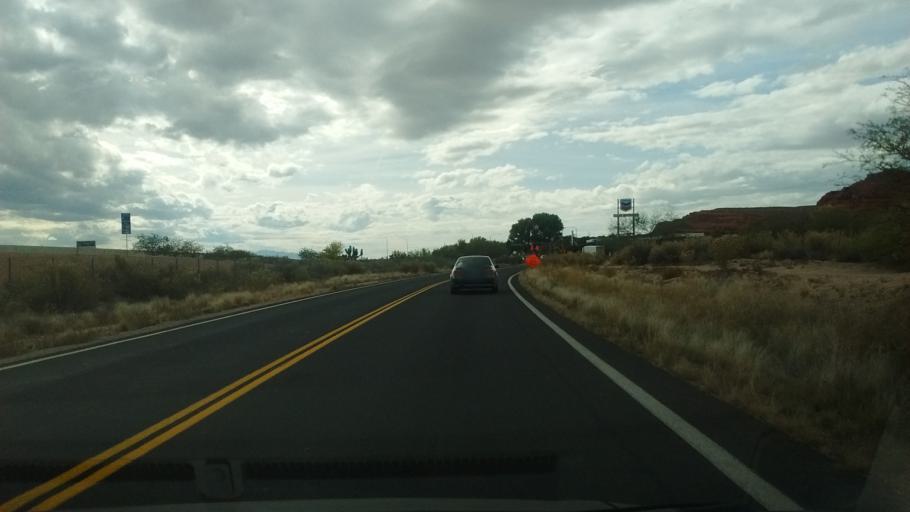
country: US
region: Utah
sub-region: Washington County
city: Washington
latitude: 37.1312
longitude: -113.5227
